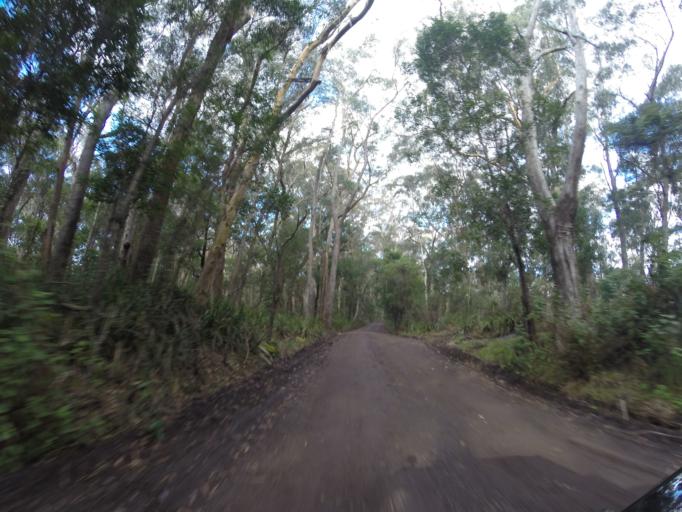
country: AU
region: New South Wales
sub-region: Wollongong
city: Cordeaux Heights
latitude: -34.4314
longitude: 150.7838
